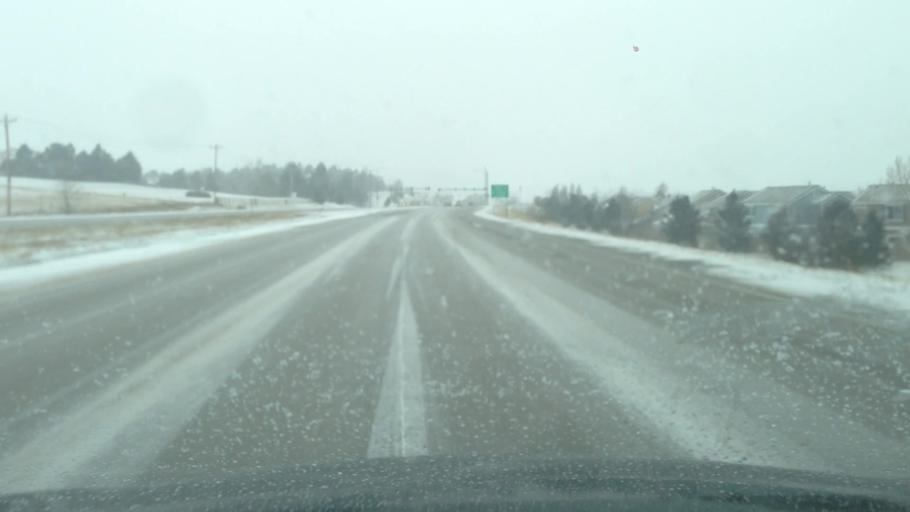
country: US
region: Colorado
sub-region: Arapahoe County
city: Dove Valley
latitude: 39.5818
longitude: -104.7943
